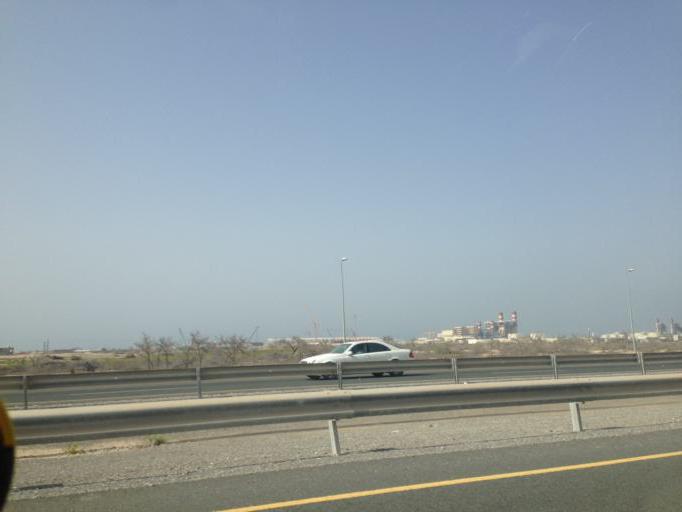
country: OM
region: Al Batinah
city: Barka'
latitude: 23.6980
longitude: 57.9709
